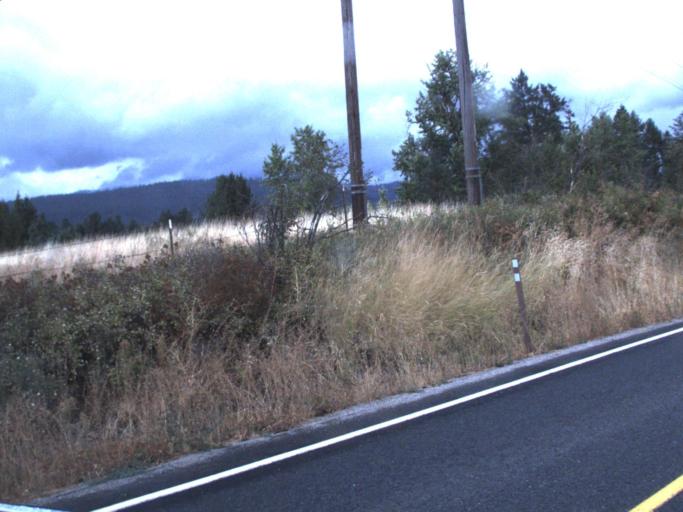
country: US
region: Washington
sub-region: Stevens County
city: Chewelah
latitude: 48.0832
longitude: -117.7579
